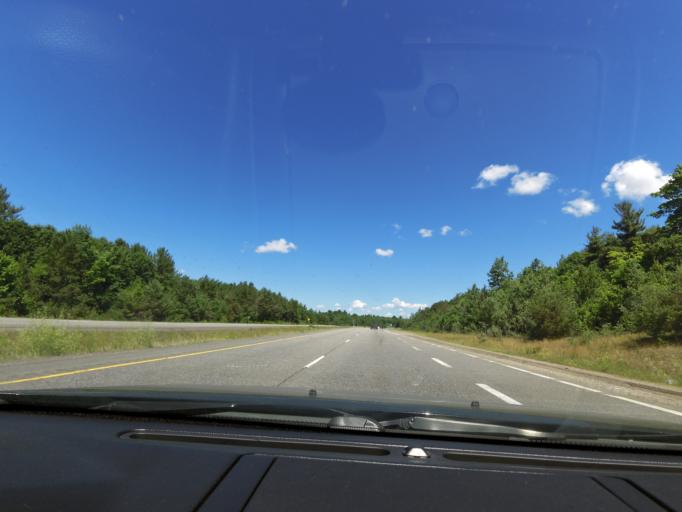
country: CA
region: Ontario
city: Bracebridge
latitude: 45.0585
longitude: -79.2939
